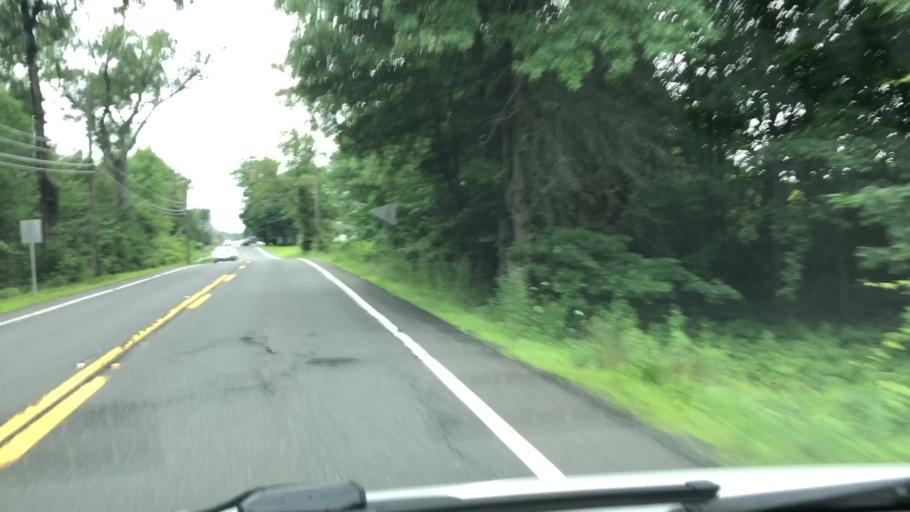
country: US
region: Massachusetts
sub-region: Franklin County
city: Whately
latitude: 42.4494
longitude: -72.6268
